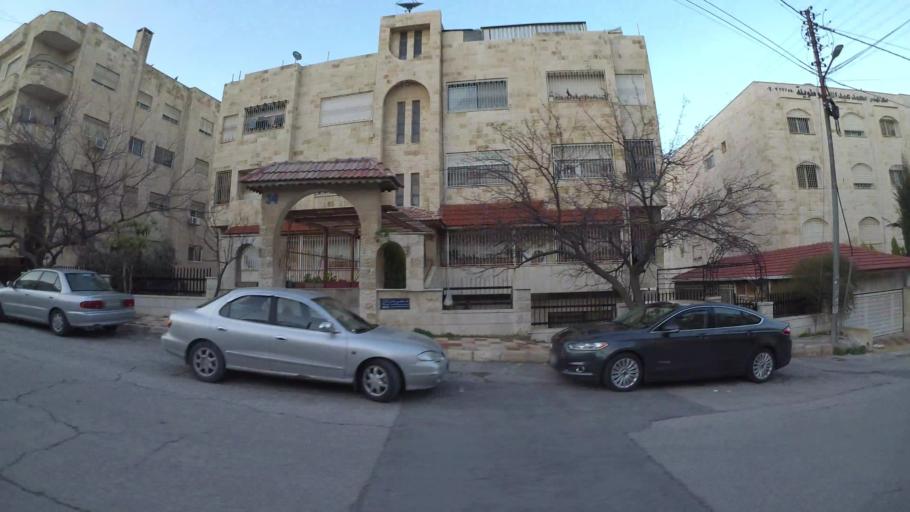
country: JO
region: Amman
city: Al Jubayhah
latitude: 31.9869
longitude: 35.8827
